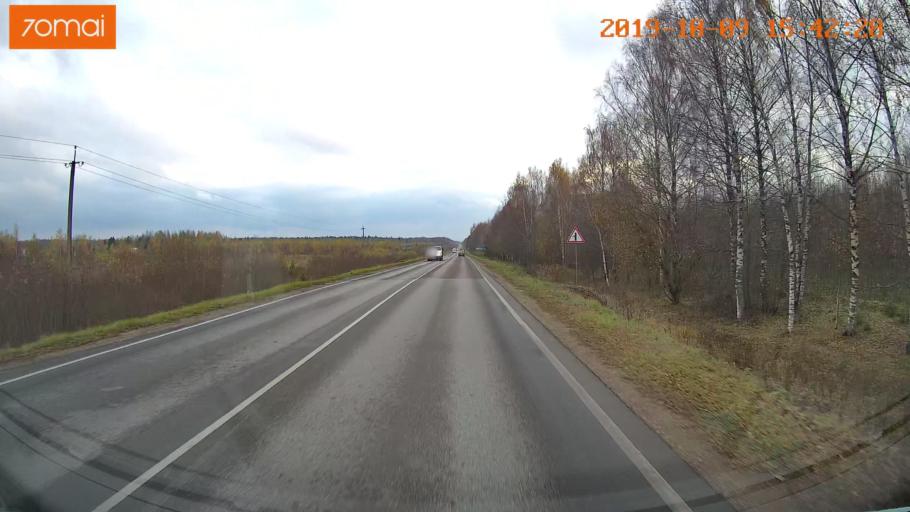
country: RU
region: Kostroma
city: Oktyabr'skiy
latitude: 57.8681
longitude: 41.1064
